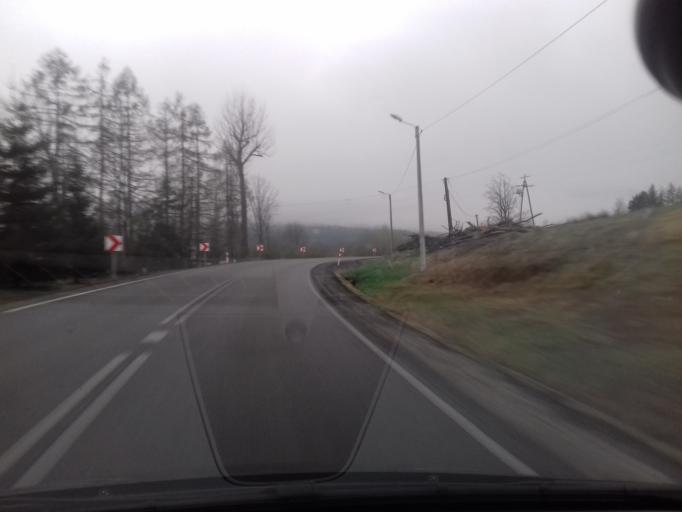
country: PL
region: Lesser Poland Voivodeship
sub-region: Powiat limanowski
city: Dobra
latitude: 49.7020
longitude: 20.2322
